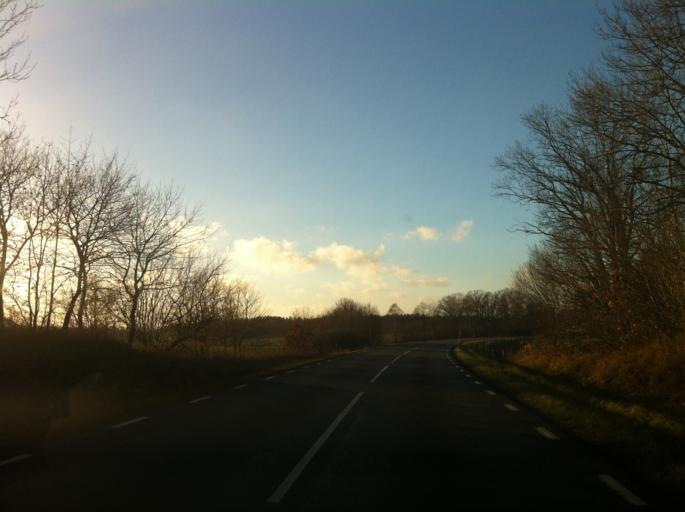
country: SE
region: Skane
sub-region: Ostra Goinge Kommun
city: Knislinge
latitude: 56.1894
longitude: 14.0305
